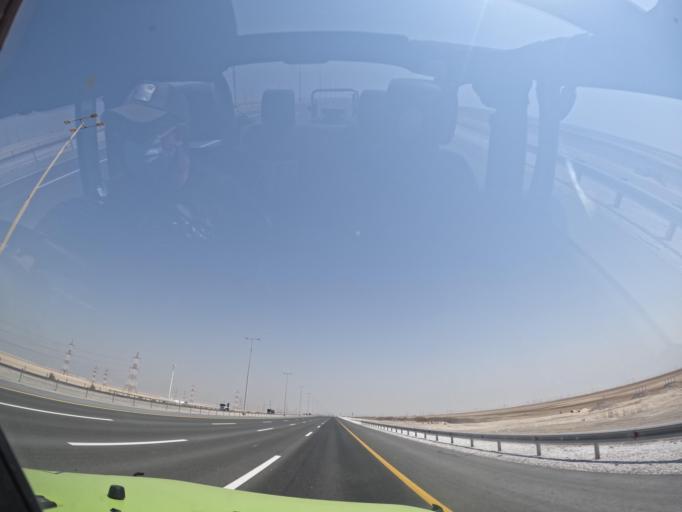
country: AE
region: Abu Dhabi
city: Abu Dhabi
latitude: 24.1542
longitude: 54.2645
